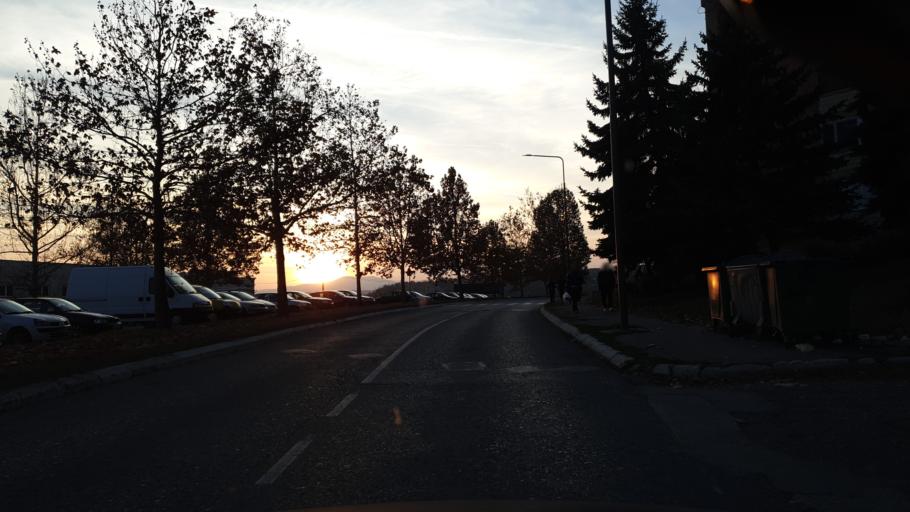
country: RS
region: Central Serbia
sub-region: Borski Okrug
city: Bor
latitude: 44.0542
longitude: 22.0983
